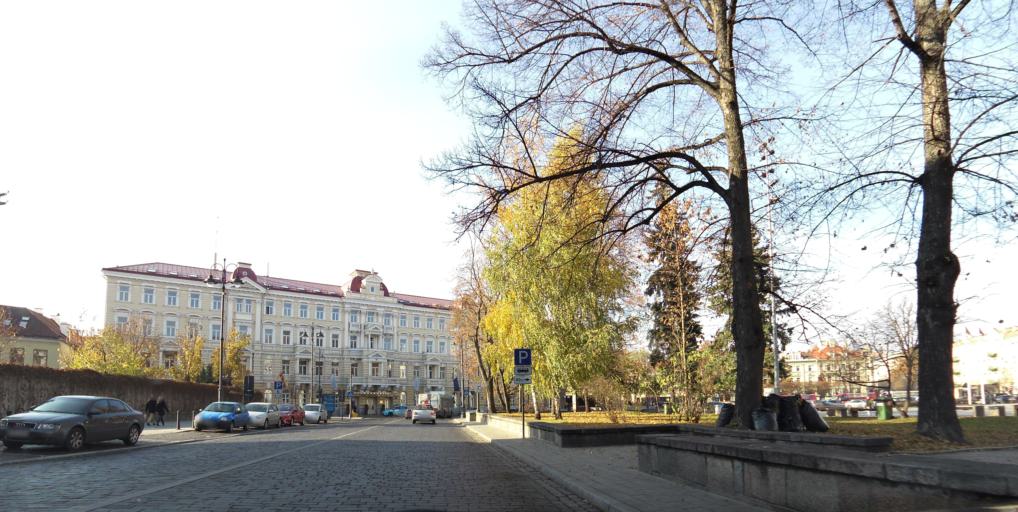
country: LT
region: Vilnius County
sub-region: Vilnius
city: Vilnius
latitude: 54.6848
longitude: 25.2871
